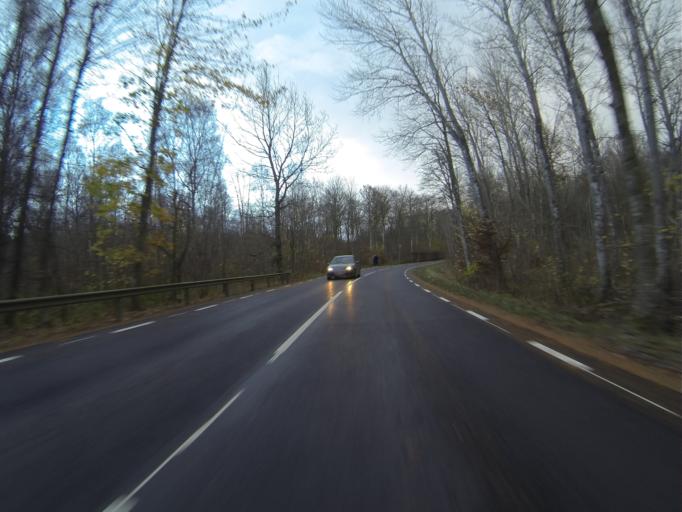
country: SE
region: Skane
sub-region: Lunds Kommun
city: Genarp
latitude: 55.5903
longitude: 13.4193
